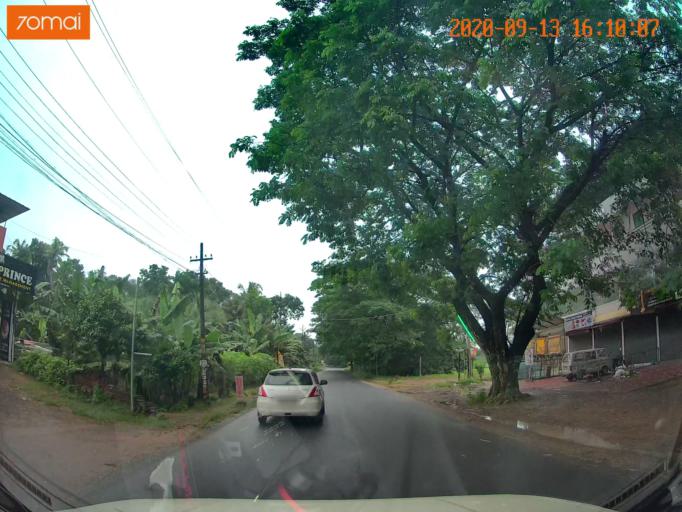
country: IN
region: Kerala
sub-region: Kottayam
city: Palackattumala
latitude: 9.6797
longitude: 76.6038
